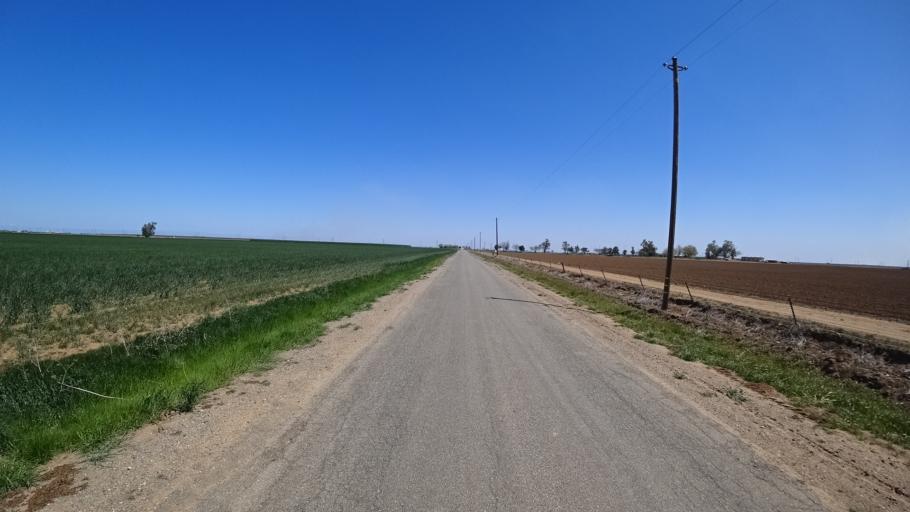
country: US
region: California
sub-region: Glenn County
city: Willows
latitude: 39.4656
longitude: -122.2826
